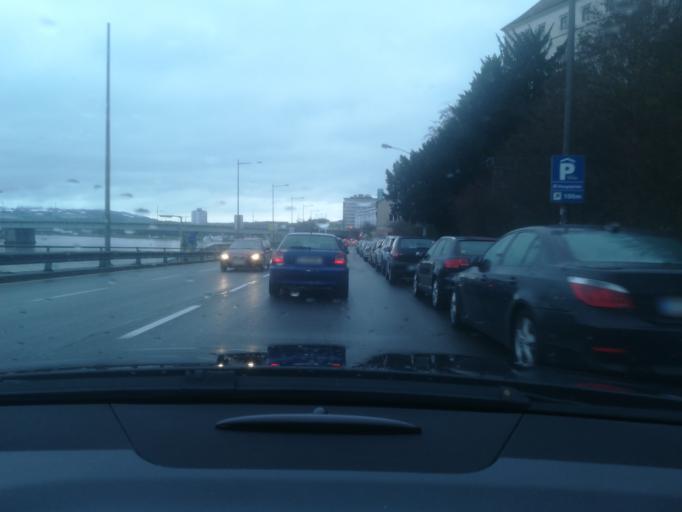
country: AT
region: Upper Austria
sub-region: Linz Stadt
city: Linz
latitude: 48.3061
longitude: 14.2812
